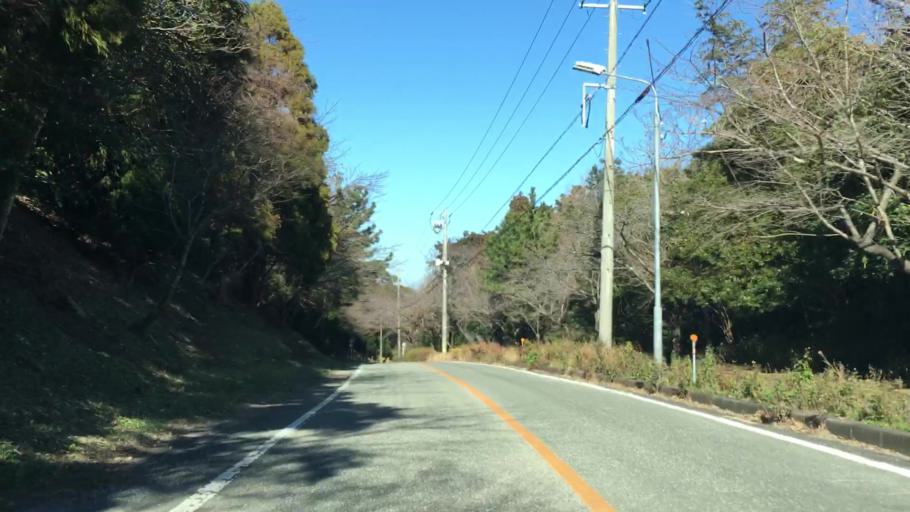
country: JP
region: Aichi
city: Tahara
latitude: 34.6752
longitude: 137.2491
